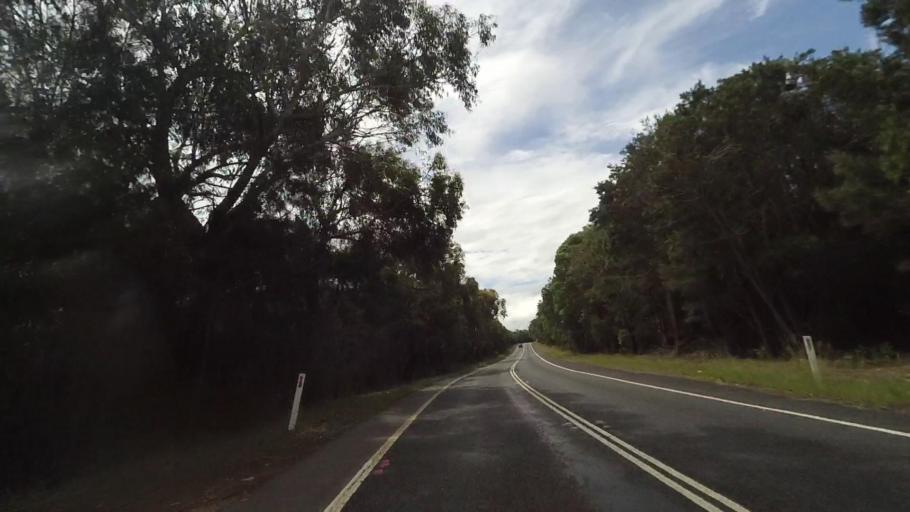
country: AU
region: New South Wales
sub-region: Sutherland Shire
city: Loftus
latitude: -34.0576
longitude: 151.0501
